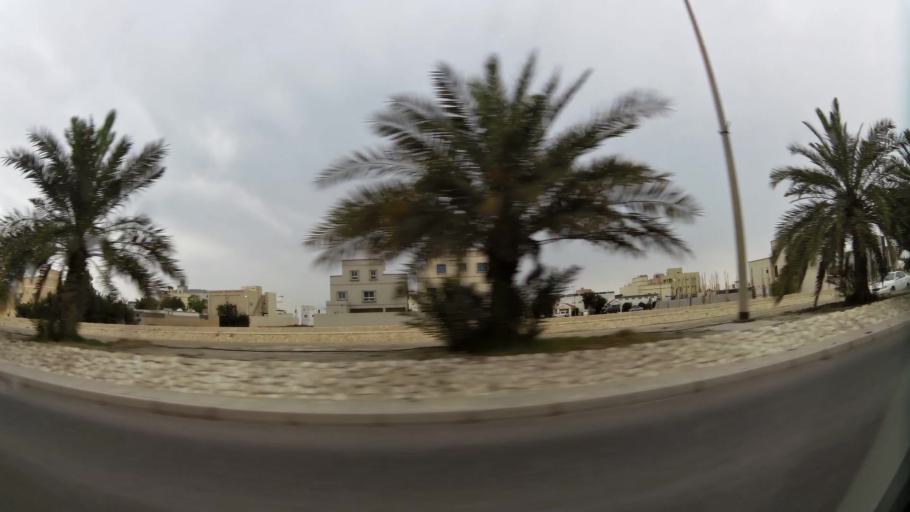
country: BH
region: Central Governorate
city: Madinat Hamad
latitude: 26.1016
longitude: 50.4989
